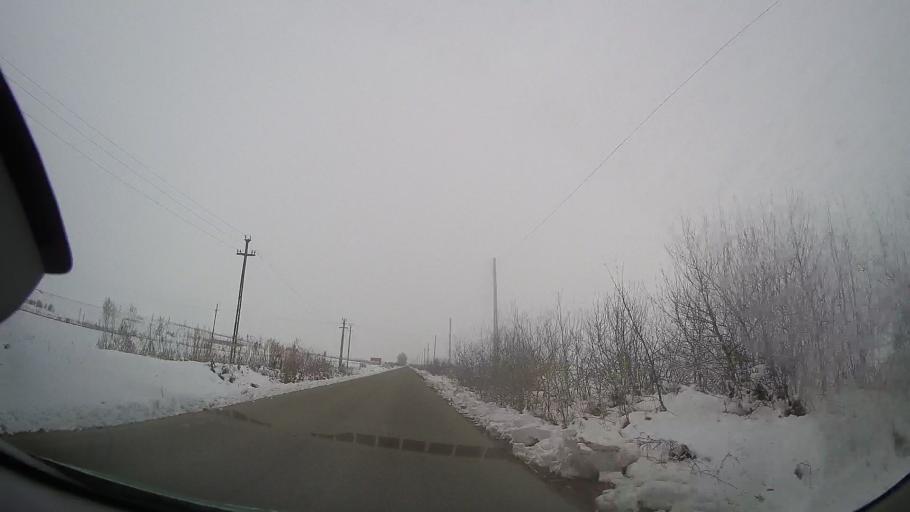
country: RO
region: Vaslui
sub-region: Comuna Todiresti
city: Todiresti
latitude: 46.8415
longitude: 27.3976
